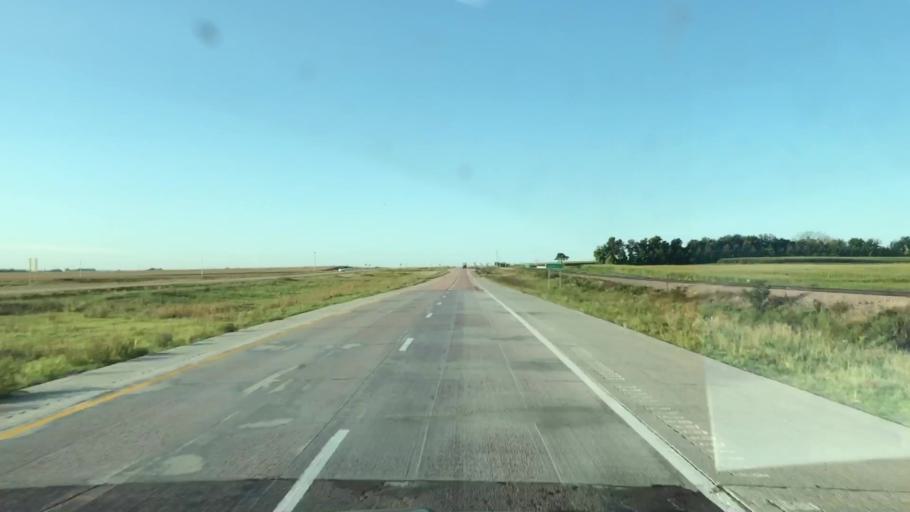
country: US
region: Iowa
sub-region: Osceola County
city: Sibley
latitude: 43.3499
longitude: -95.7721
